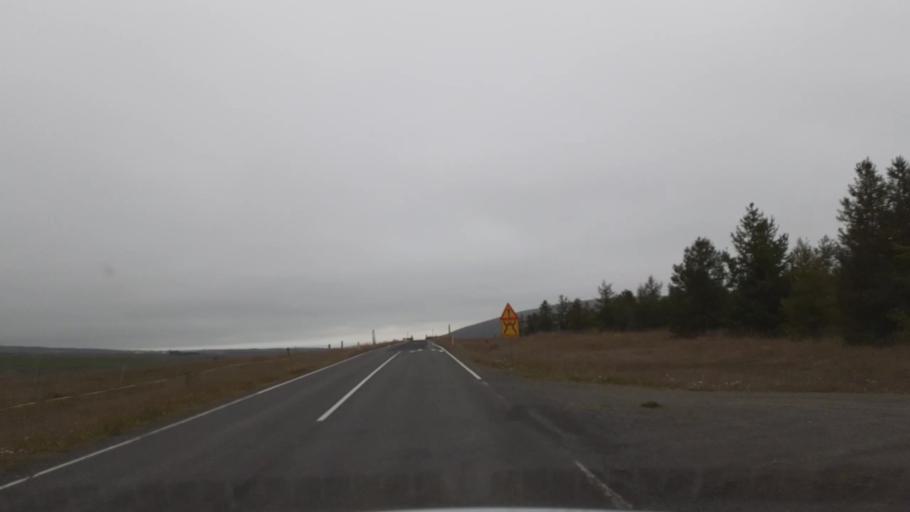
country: IS
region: Northeast
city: Siglufjoerdur
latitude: 65.7387
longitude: -19.1342
